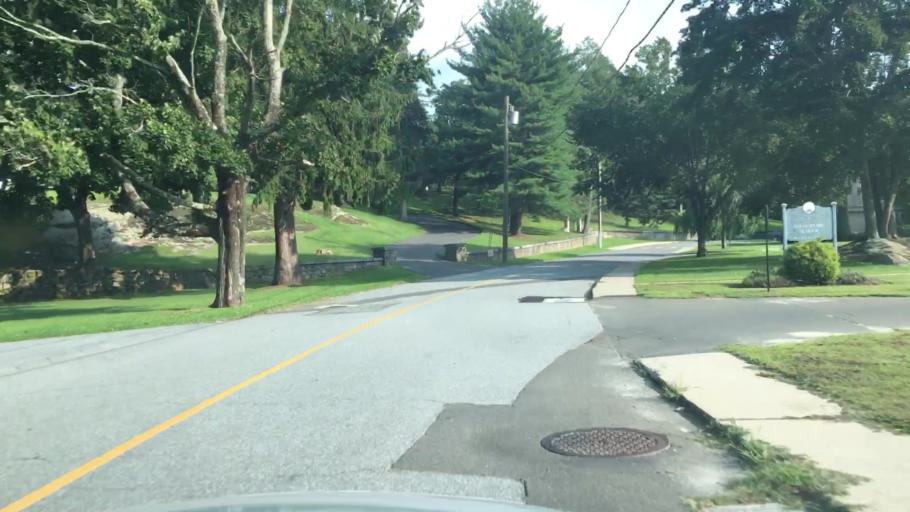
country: US
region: Connecticut
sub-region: Middlesex County
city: Deep River Center
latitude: 41.3867
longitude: -72.4329
